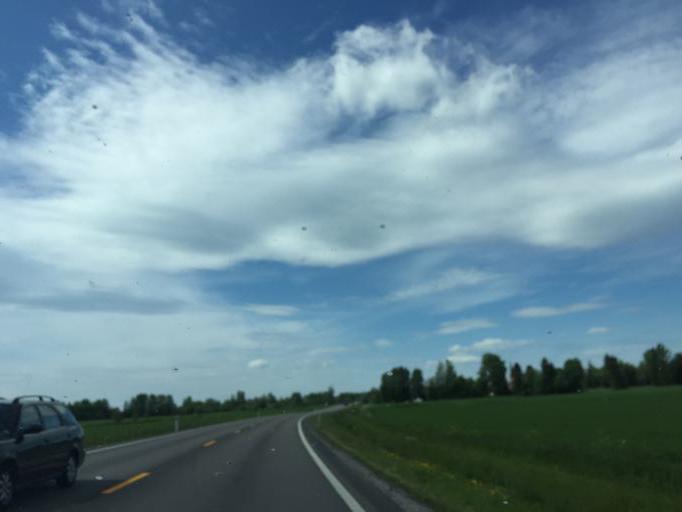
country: NO
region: Akershus
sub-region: Nes
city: Arnes
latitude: 60.1636
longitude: 11.4611
